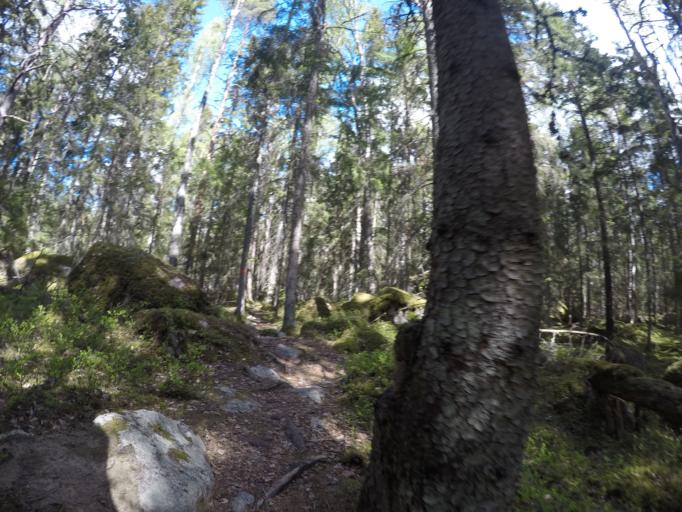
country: SE
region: Soedermanland
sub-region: Eskilstuna Kommun
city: Hallbybrunn
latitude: 59.3540
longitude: 16.4017
